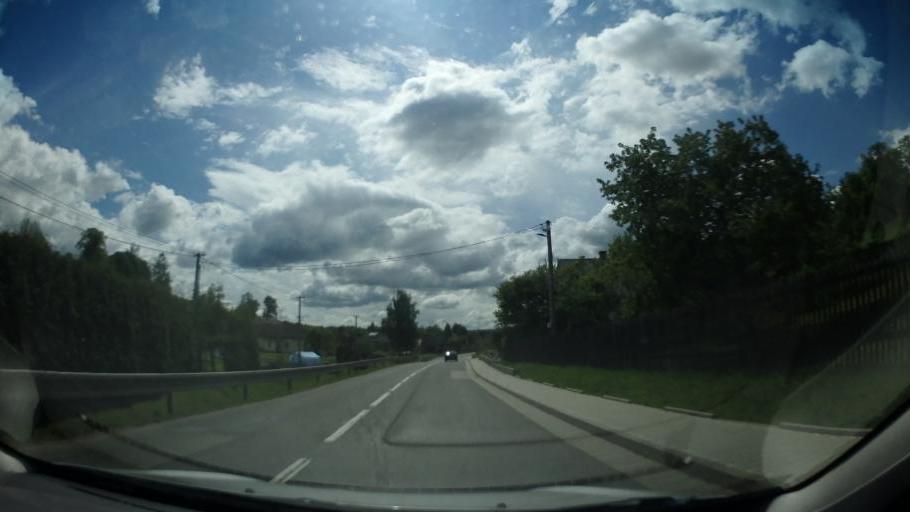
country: CZ
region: Pardubicky
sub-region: Okres Svitavy
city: Moravska Trebova
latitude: 49.6994
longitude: 16.6412
